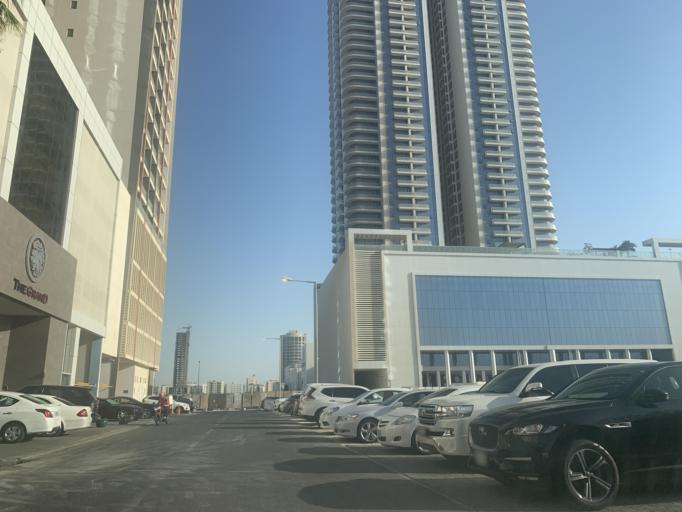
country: BH
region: Manama
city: Jidd Hafs
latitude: 26.2368
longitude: 50.5563
